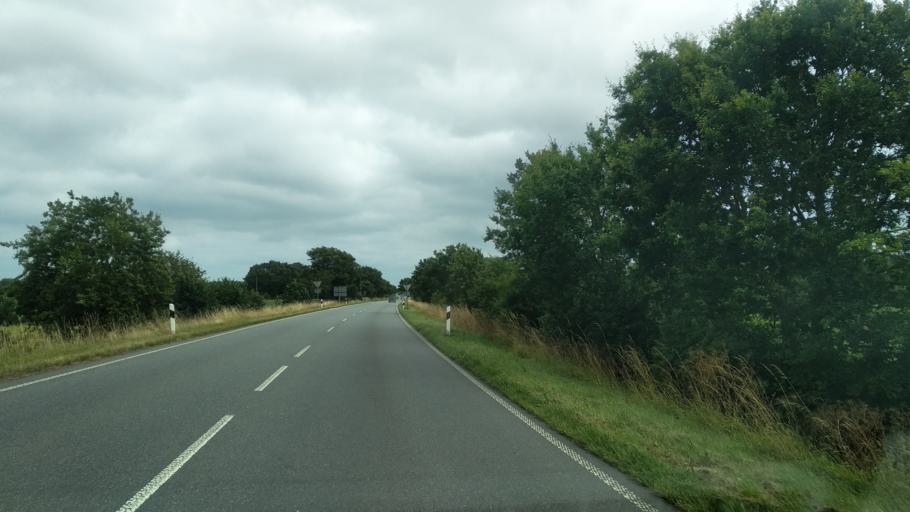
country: DE
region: Schleswig-Holstein
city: Neuberend
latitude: 54.5471
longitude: 9.5445
